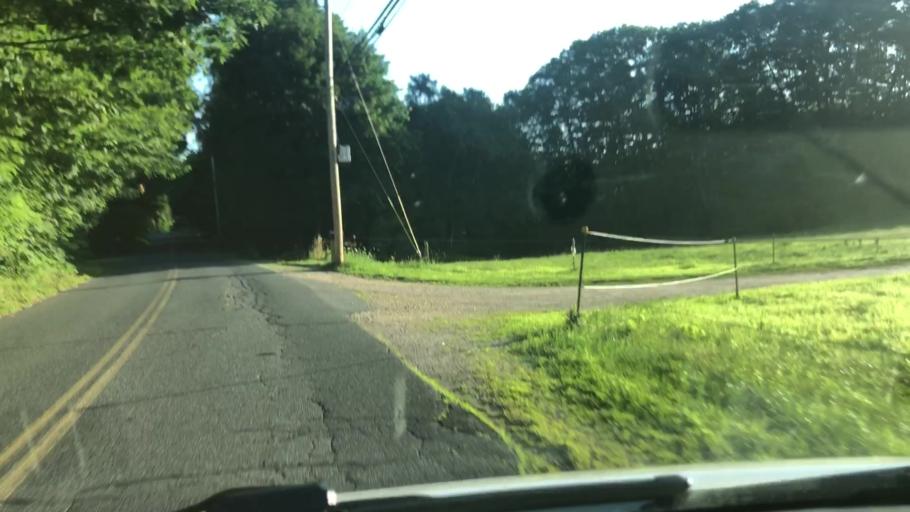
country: US
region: Massachusetts
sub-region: Hampshire County
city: Williamsburg
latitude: 42.3764
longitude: -72.7309
